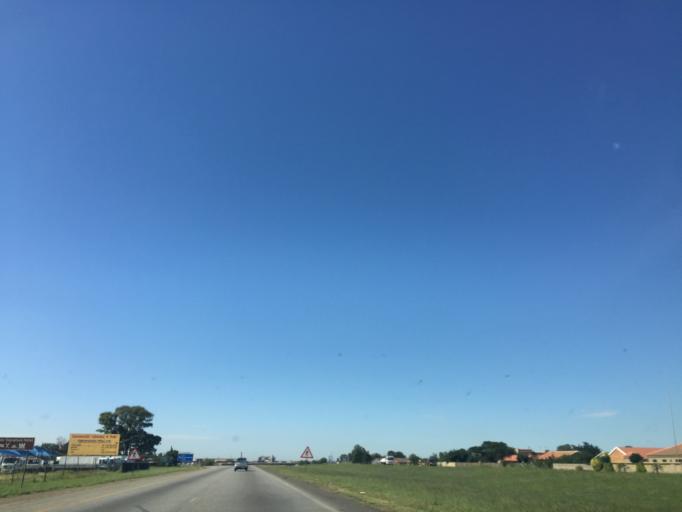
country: ZA
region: Gauteng
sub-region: Sedibeng District Municipality
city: Meyerton
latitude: -26.5548
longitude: 28.0025
